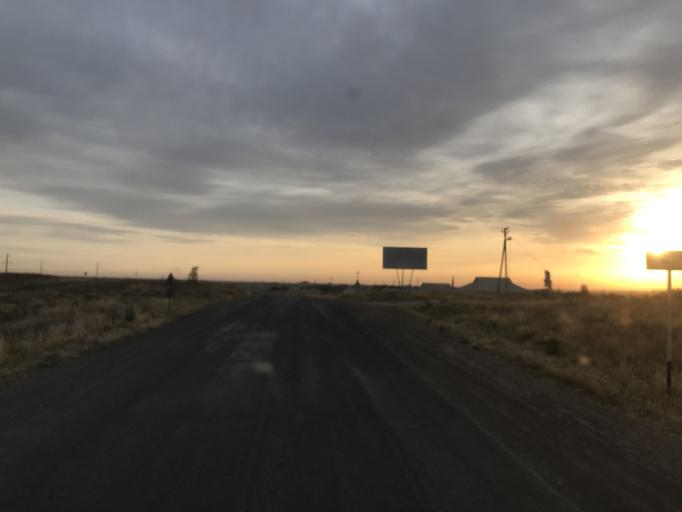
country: UZ
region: Toshkent
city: Amir Timur
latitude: 41.2281
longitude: 68.8065
